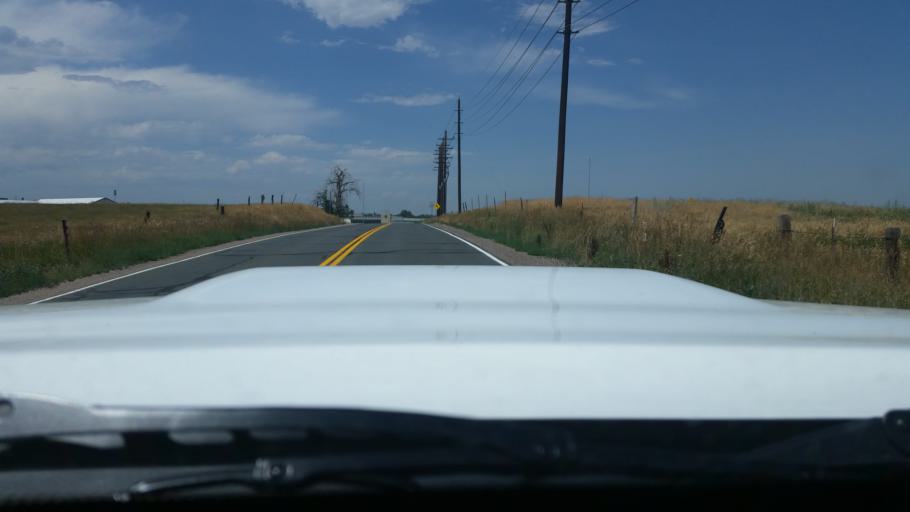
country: US
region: Colorado
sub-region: Broomfield County
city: Broomfield
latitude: 39.8980
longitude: -105.0811
